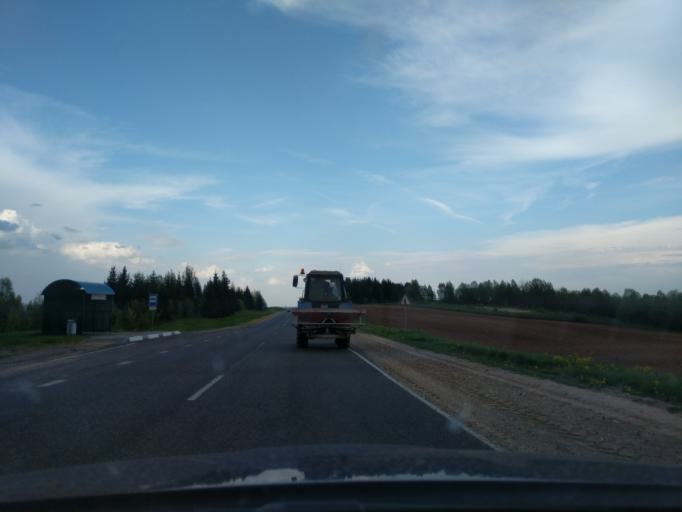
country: BY
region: Grodnenskaya
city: Navahrudak
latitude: 53.6451
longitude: 25.9272
